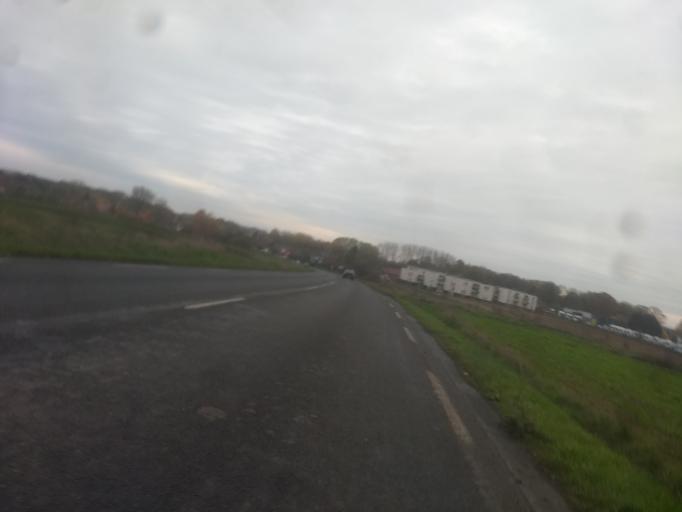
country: FR
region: Nord-Pas-de-Calais
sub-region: Departement du Pas-de-Calais
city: Achicourt
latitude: 50.2686
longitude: 2.7493
